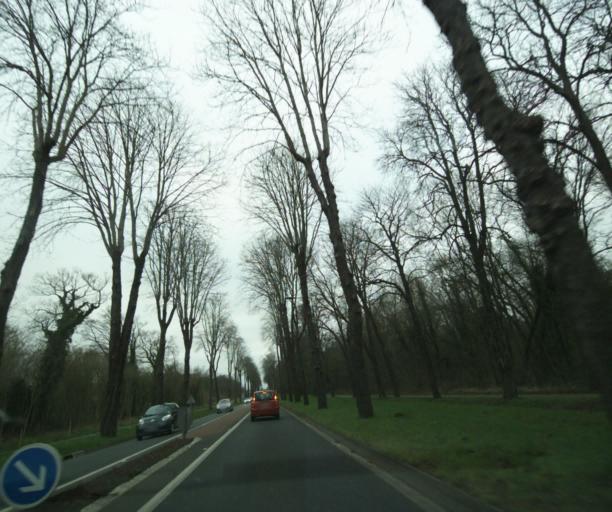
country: FR
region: Ile-de-France
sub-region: Departement des Yvelines
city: Poissy
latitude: 48.9206
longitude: 2.0587
